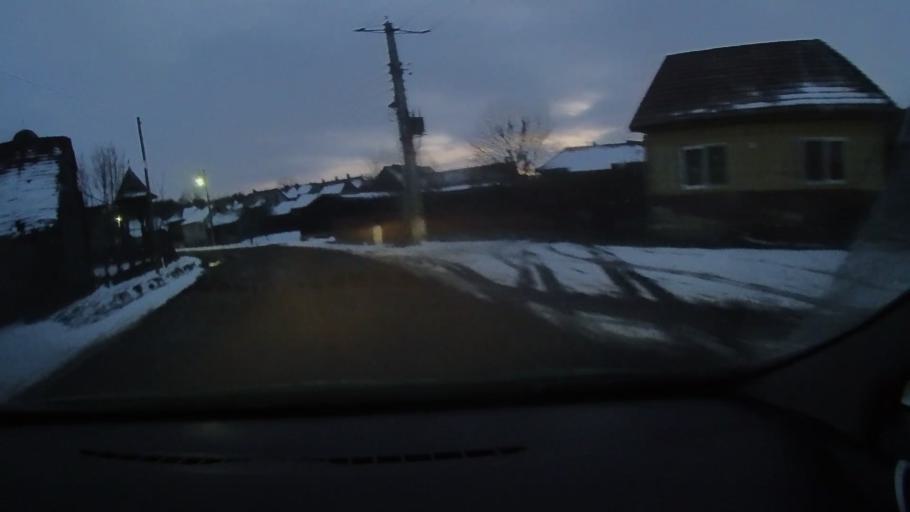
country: RO
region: Harghita
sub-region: Comuna Darjiu
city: Darjiu
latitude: 46.1729
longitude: 25.2339
